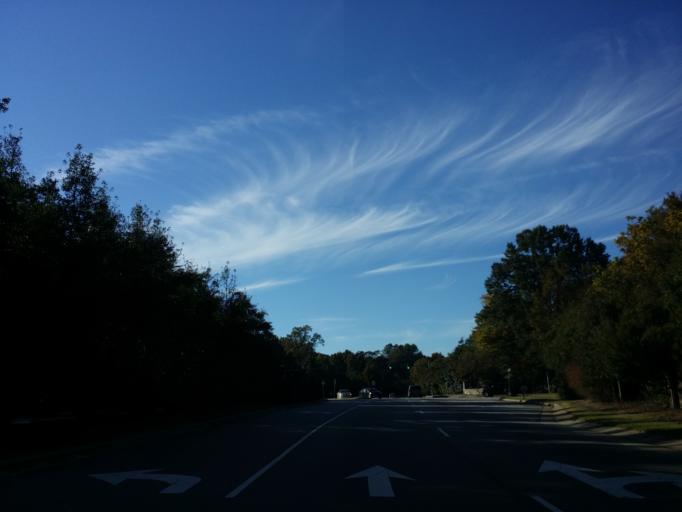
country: US
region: North Carolina
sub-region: Wake County
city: Raleigh
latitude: 35.7712
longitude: -78.6522
